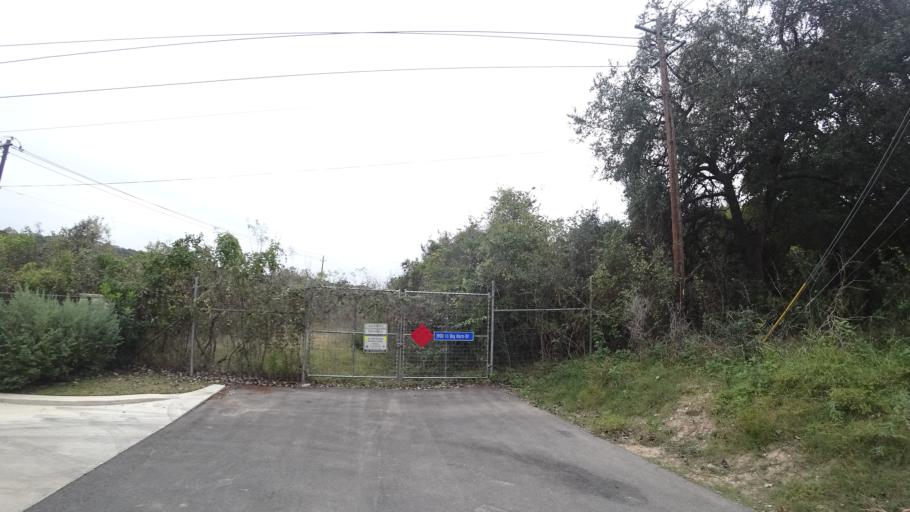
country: US
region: Texas
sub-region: Travis County
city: Hudson Bend
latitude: 30.3682
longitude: -97.9156
